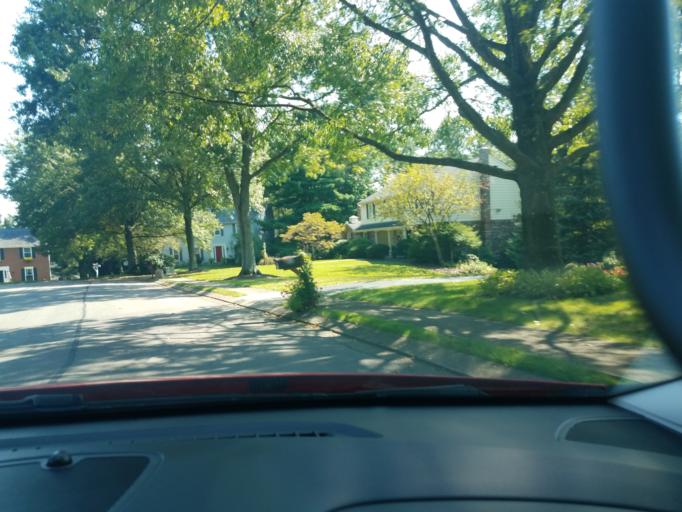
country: US
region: Pennsylvania
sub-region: Allegheny County
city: Franklin Park
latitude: 40.5680
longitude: -80.0752
